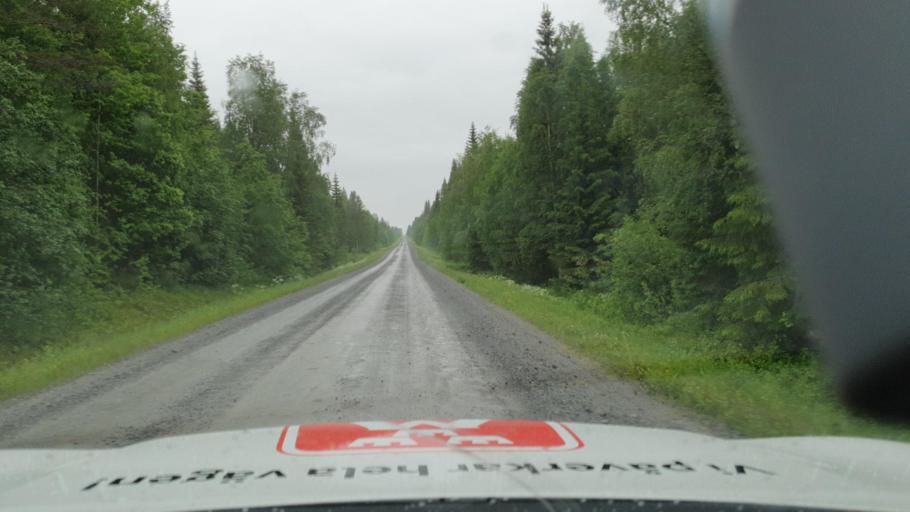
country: SE
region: Vaesterbotten
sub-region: Nordmalings Kommun
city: Nordmaling
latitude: 63.8441
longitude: 19.4798
